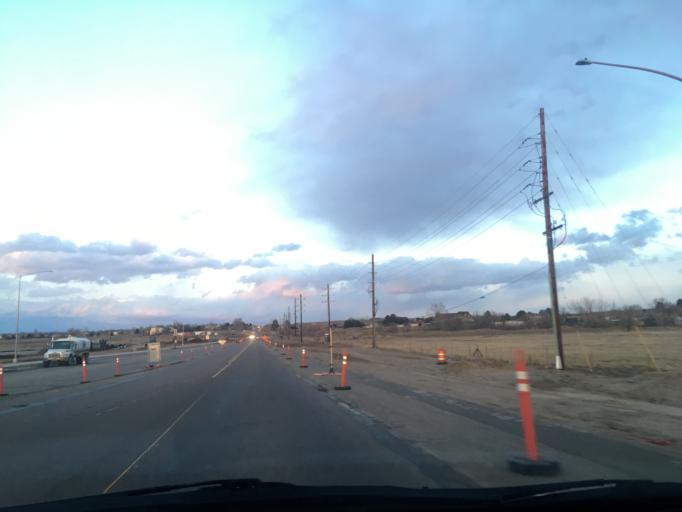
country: US
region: Colorado
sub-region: Adams County
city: Northglenn
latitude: 39.9575
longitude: -104.9759
